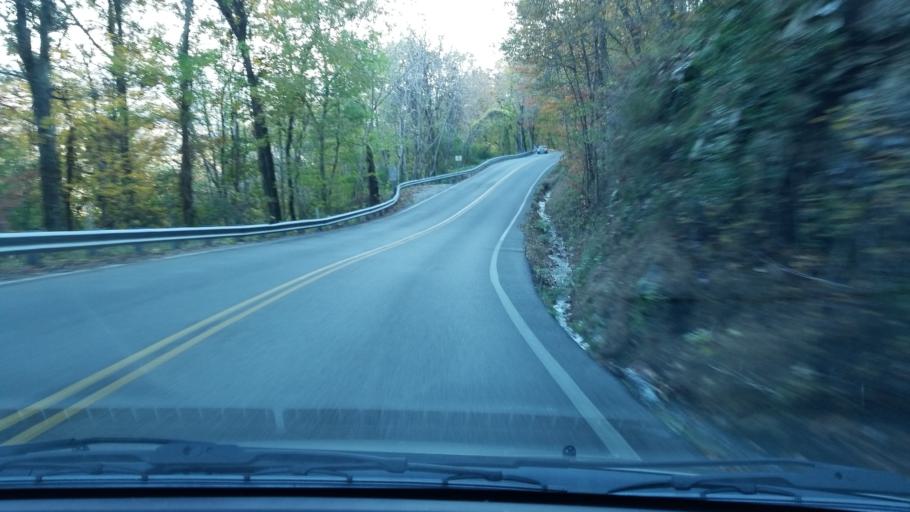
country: US
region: Tennessee
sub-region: Hamilton County
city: Falling Water
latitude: 35.2133
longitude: -85.2606
